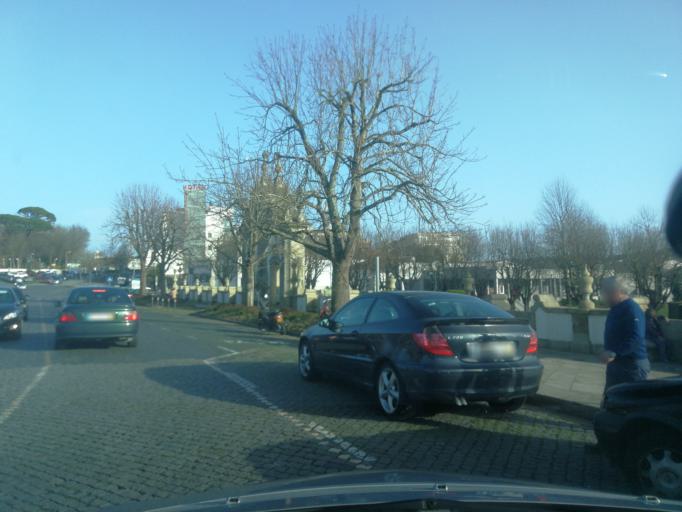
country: PT
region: Braga
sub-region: Barcelos
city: Barcelos
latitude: 41.5315
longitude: -8.6188
